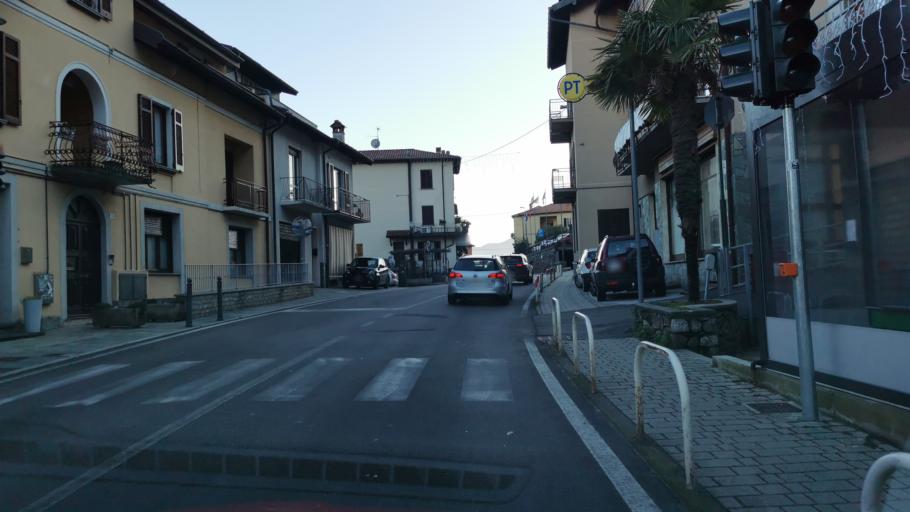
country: IT
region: Lombardy
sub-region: Provincia di Como
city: San Siro
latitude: 46.0542
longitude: 9.2590
